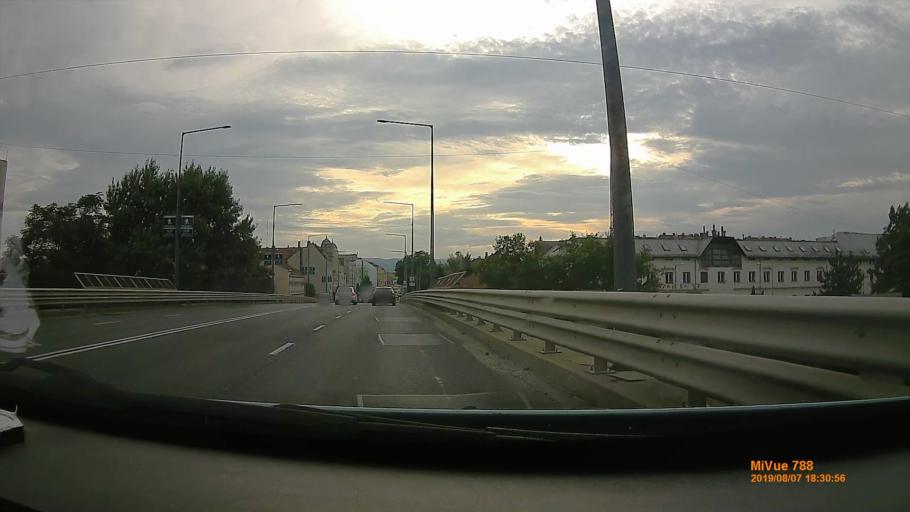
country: HU
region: Borsod-Abauj-Zemplen
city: Miskolc
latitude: 48.1052
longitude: 20.8014
